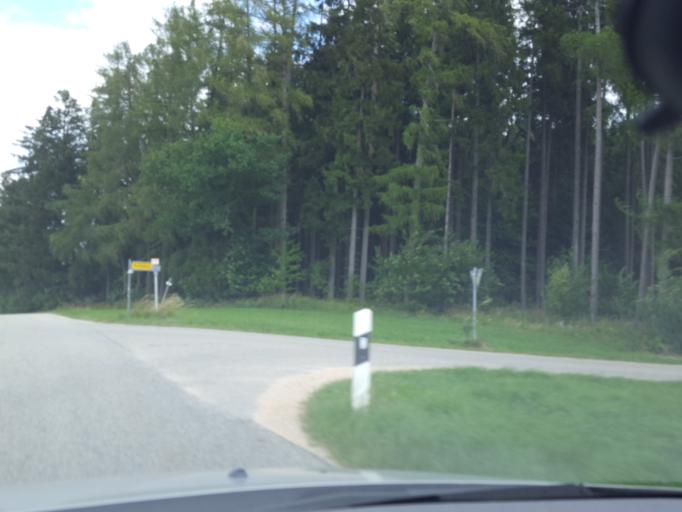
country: DE
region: Bavaria
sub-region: Upper Bavaria
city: Neumarkt-Sankt Veit
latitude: 48.3781
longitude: 12.4908
